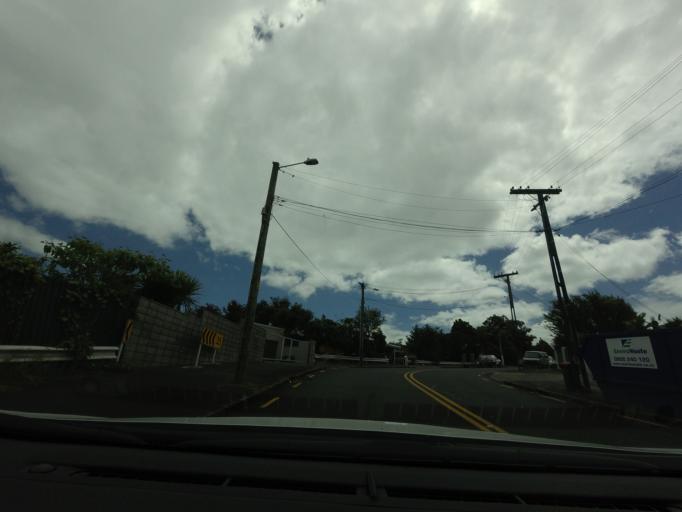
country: NZ
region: Auckland
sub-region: Auckland
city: Auckland
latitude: -36.8656
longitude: 174.7332
